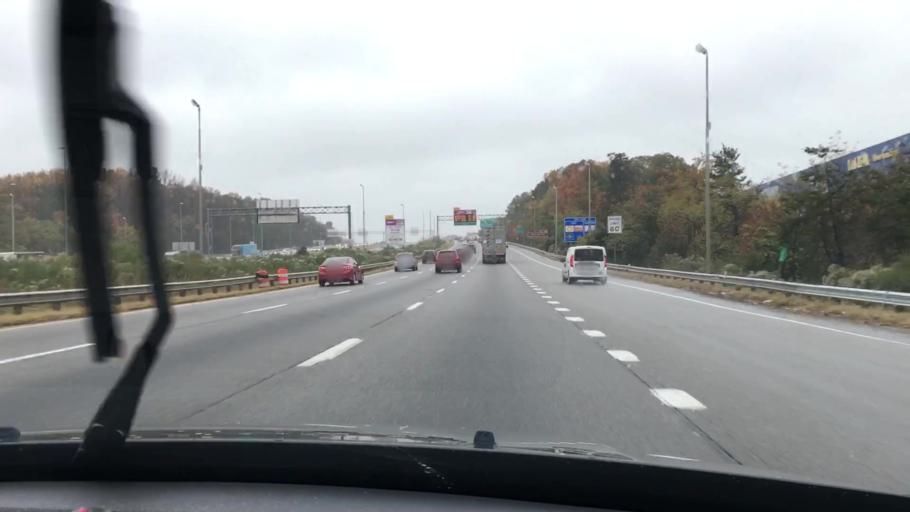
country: US
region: Virginia
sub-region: Prince William County
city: Potomac Mills
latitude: 38.6451
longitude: -77.2865
